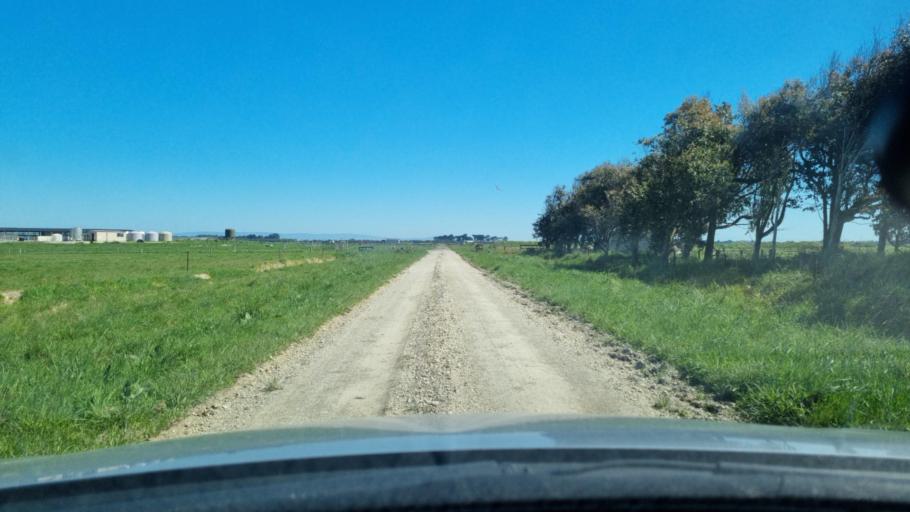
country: NZ
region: Southland
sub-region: Invercargill City
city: Invercargill
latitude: -46.4225
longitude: 168.3128
